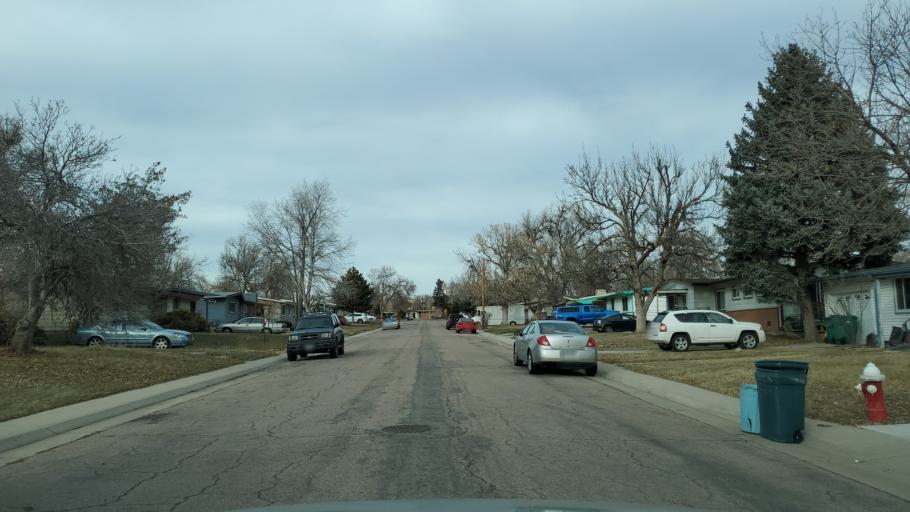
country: US
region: Colorado
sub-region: Adams County
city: Sherrelwood
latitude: 39.8380
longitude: -105.0165
